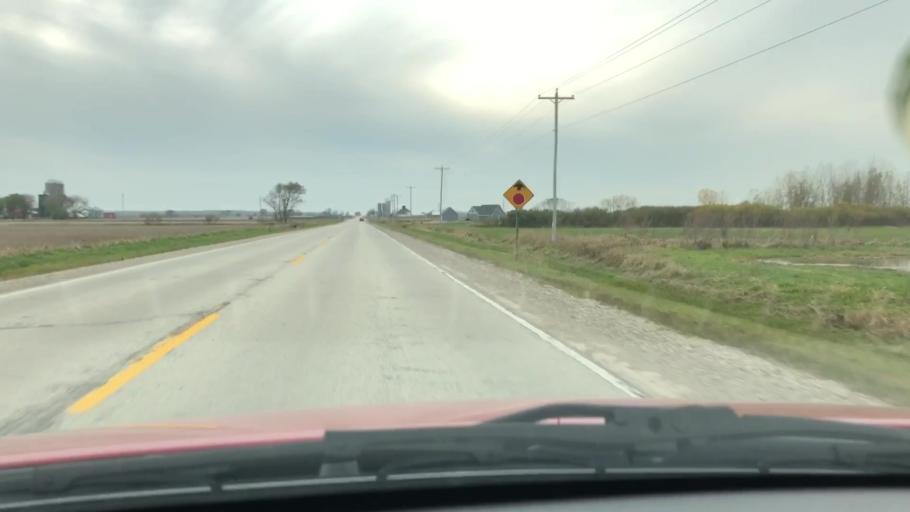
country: US
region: Wisconsin
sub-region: Outagamie County
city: Seymour
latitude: 44.4439
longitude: -88.2856
